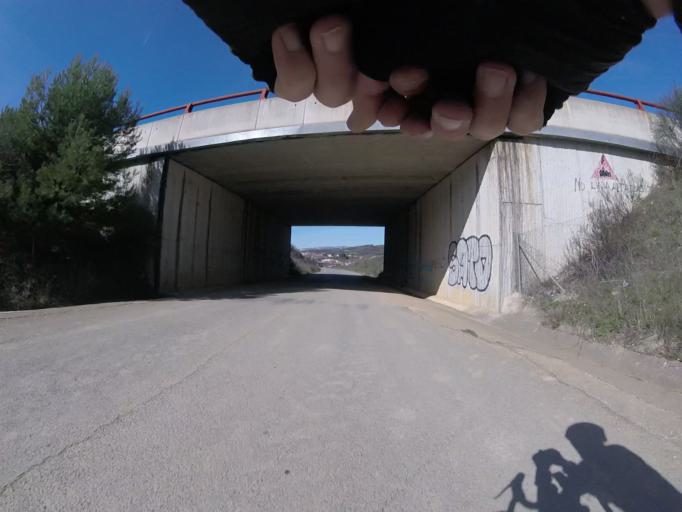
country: ES
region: Navarre
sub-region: Provincia de Navarra
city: Villatuerta
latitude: 42.6576
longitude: -1.9855
